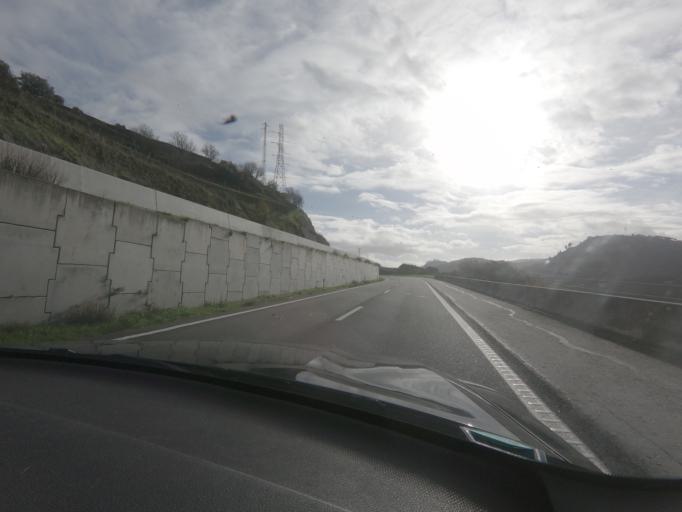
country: PT
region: Vila Real
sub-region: Peso da Regua
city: Peso da Regua
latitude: 41.1453
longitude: -7.7749
